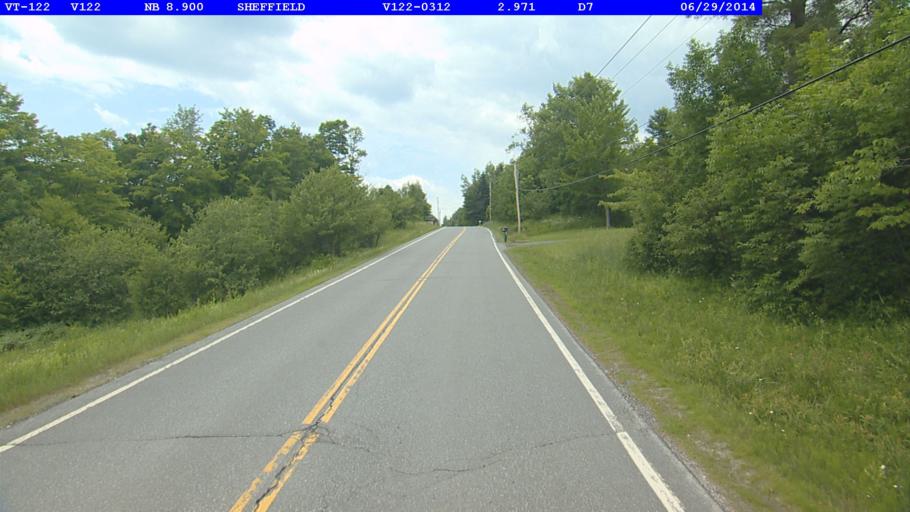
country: US
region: Vermont
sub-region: Caledonia County
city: Lyndonville
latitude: 44.6217
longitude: -72.1267
